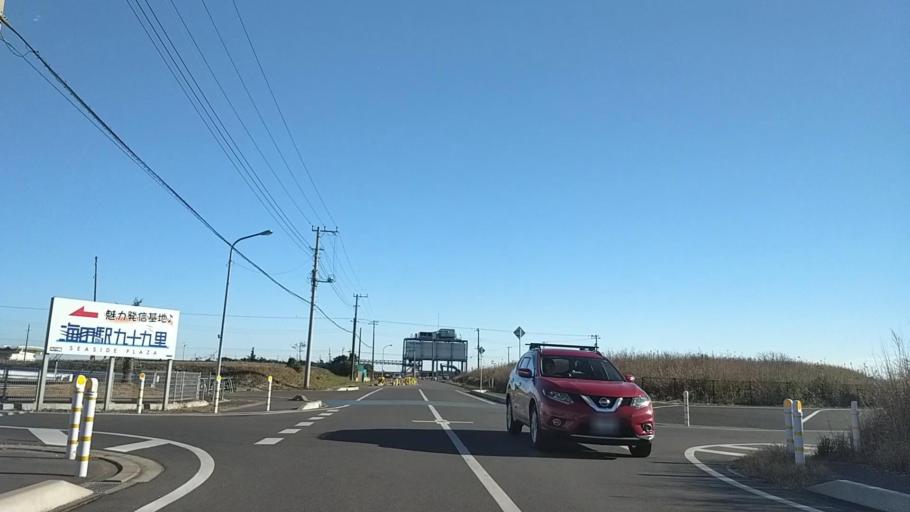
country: JP
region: Chiba
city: Naruto
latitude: 35.5374
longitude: 140.4563
